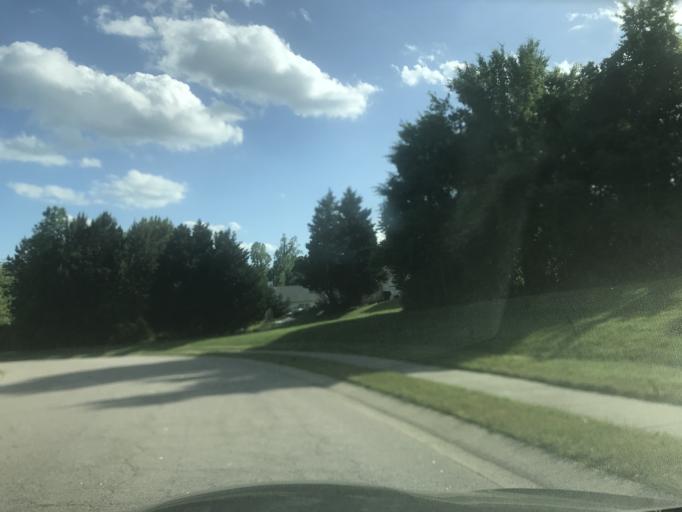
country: US
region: North Carolina
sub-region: Wake County
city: Knightdale
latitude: 35.8454
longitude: -78.5521
